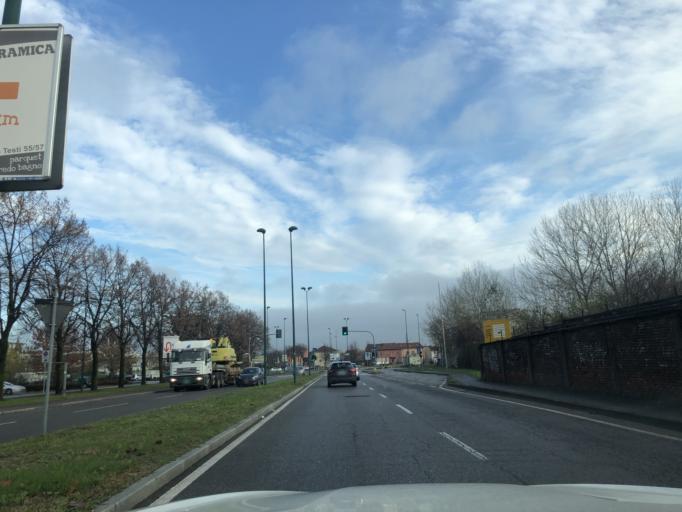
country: IT
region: Lombardy
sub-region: Citta metropolitana di Milano
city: Sesto San Giovanni
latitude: 45.5461
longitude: 9.2552
